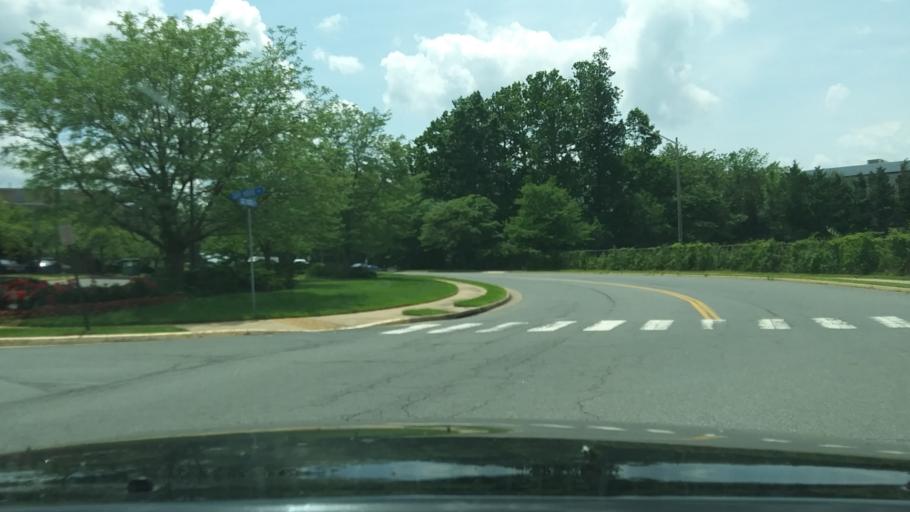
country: US
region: Virginia
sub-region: Fairfax County
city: Merrifield
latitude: 38.8669
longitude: -77.2304
